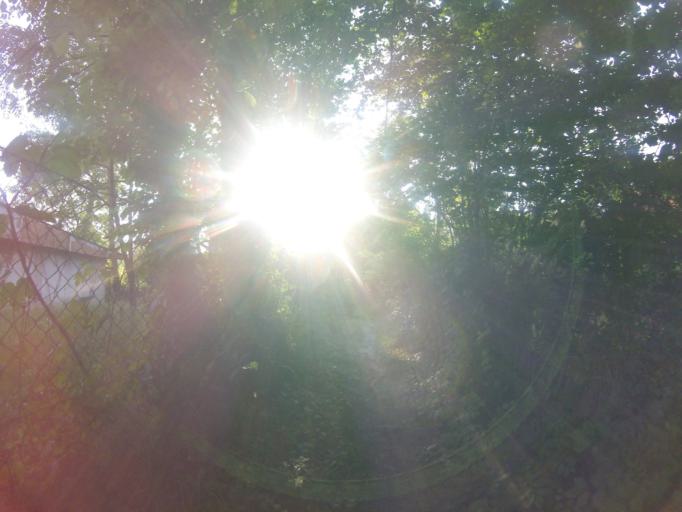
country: HU
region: Pest
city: Rackeve
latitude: 47.1906
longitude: 18.9539
